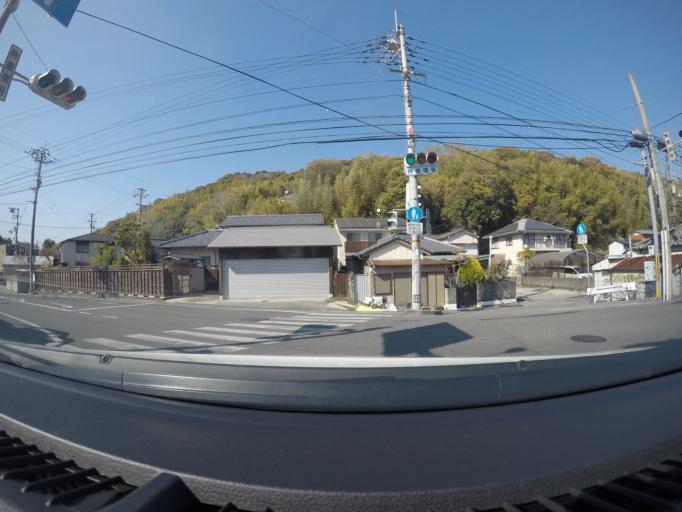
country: JP
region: Kochi
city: Kochi-shi
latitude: 33.5425
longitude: 133.5745
